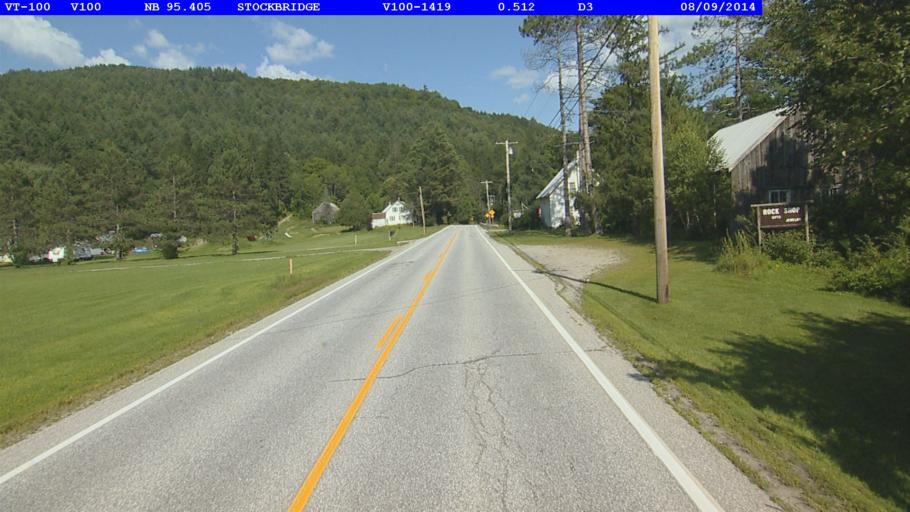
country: US
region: Vermont
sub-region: Orange County
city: Randolph
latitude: 43.7793
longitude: -72.7884
